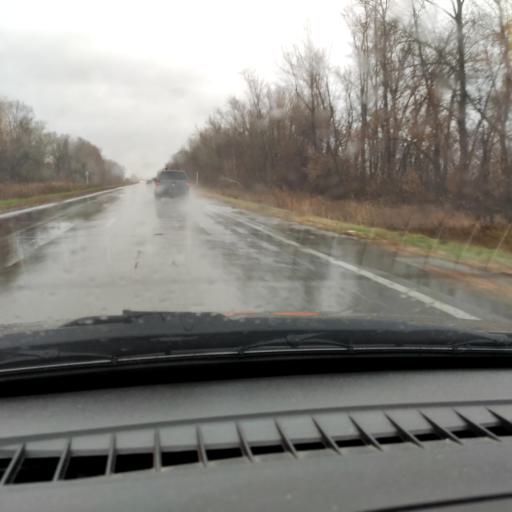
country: RU
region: Samara
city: Tol'yatti
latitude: 53.6251
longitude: 49.3067
